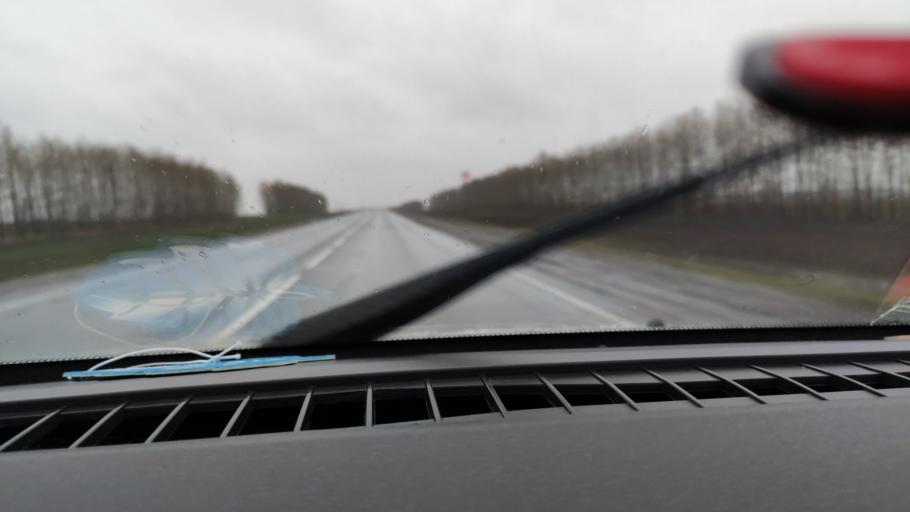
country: RU
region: Tatarstan
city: Mendeleyevsk
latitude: 55.9280
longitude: 52.2794
